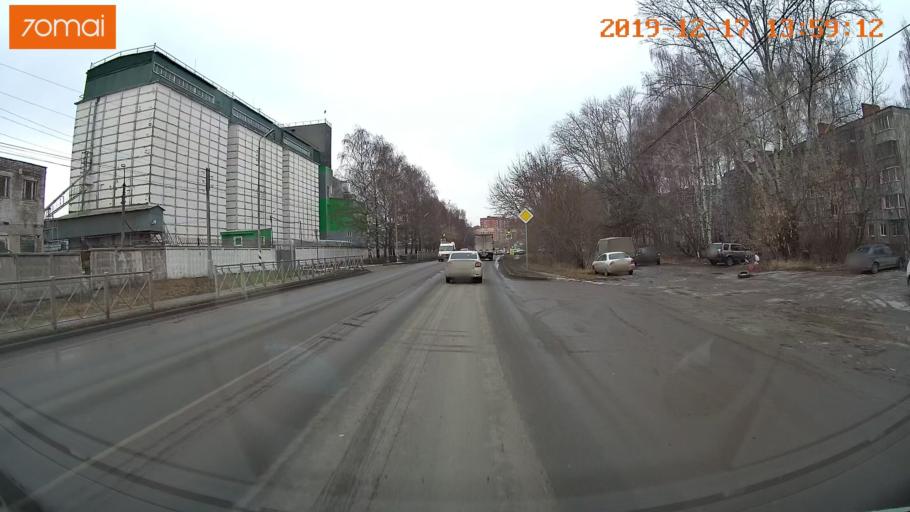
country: RU
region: Rjazan
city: Ryazan'
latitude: 54.6210
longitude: 39.6786
